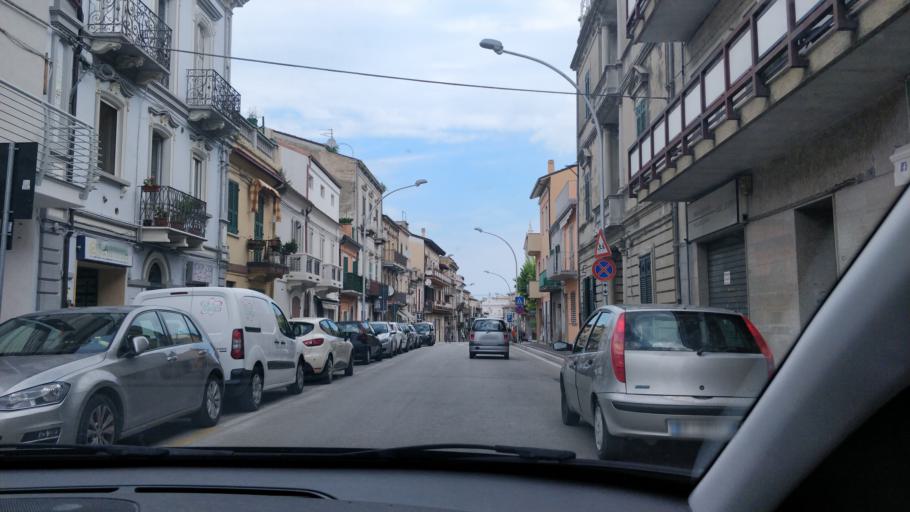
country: IT
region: Abruzzo
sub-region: Provincia di Chieti
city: Marina di San Vito
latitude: 42.2993
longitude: 14.4444
